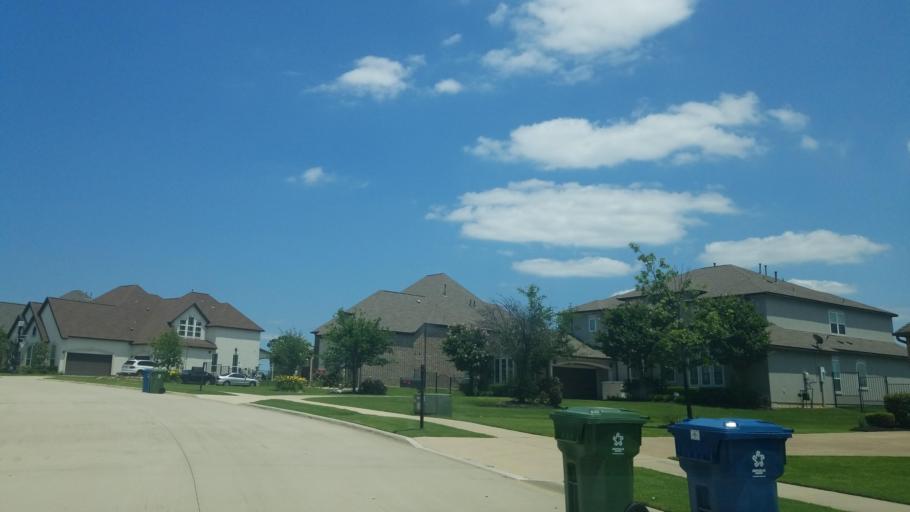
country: US
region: Texas
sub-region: Denton County
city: Copper Canyon
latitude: 33.0750
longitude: -97.0894
